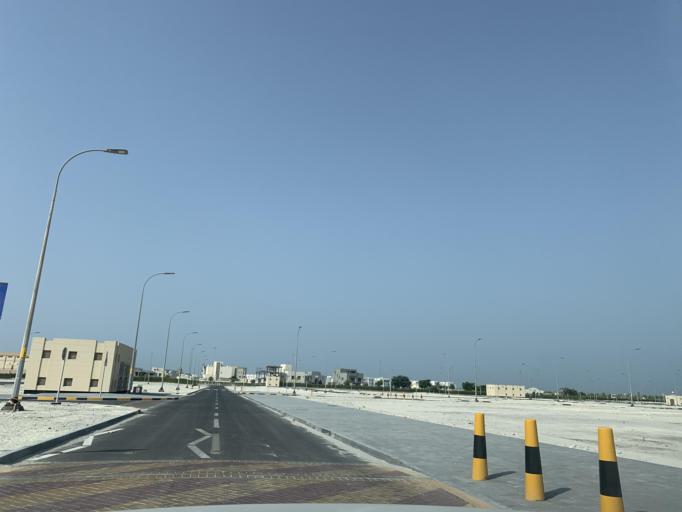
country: BH
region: Muharraq
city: Al Muharraq
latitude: 26.3068
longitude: 50.6319
